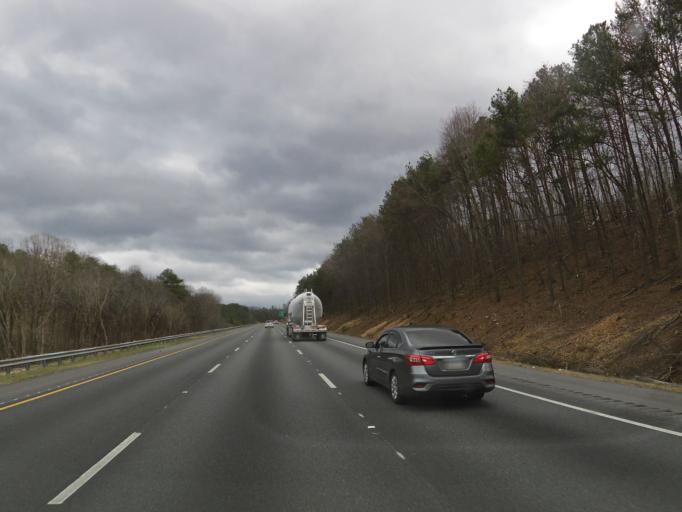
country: US
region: Georgia
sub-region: Catoosa County
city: Indian Springs
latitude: 34.9390
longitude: -85.1642
